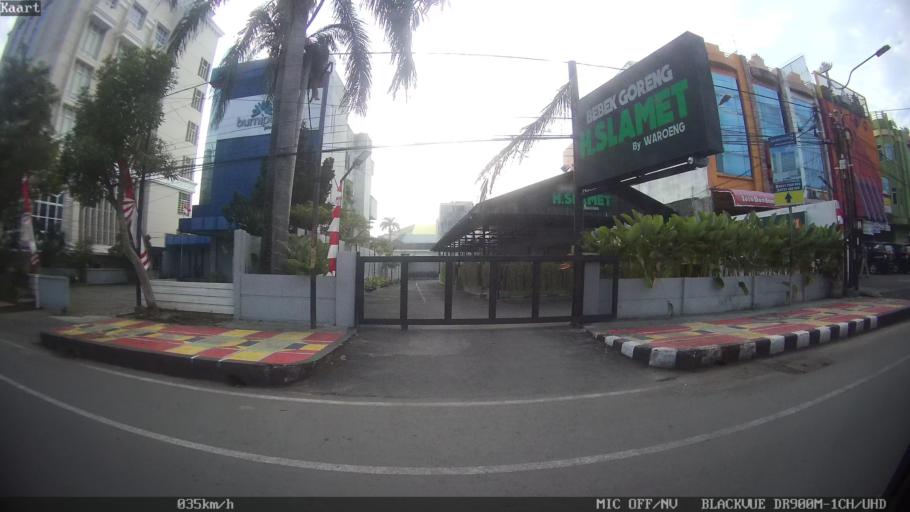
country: ID
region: Lampung
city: Bandarlampung
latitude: -5.4204
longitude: 105.2583
